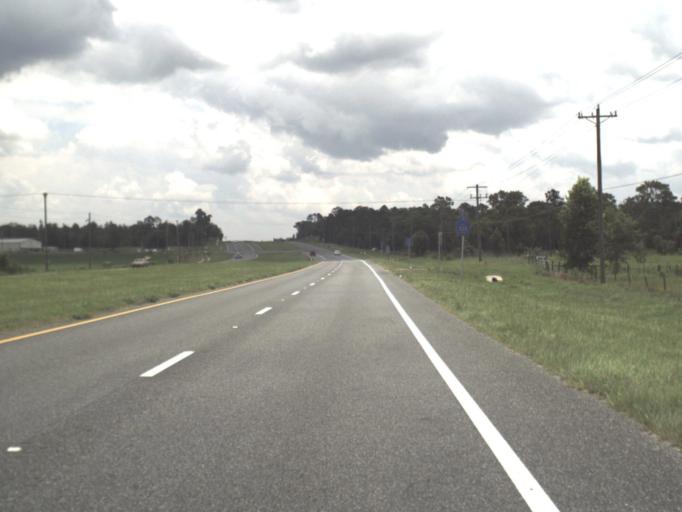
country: US
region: Florida
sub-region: Levy County
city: East Bronson
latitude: 29.4288
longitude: -82.5998
